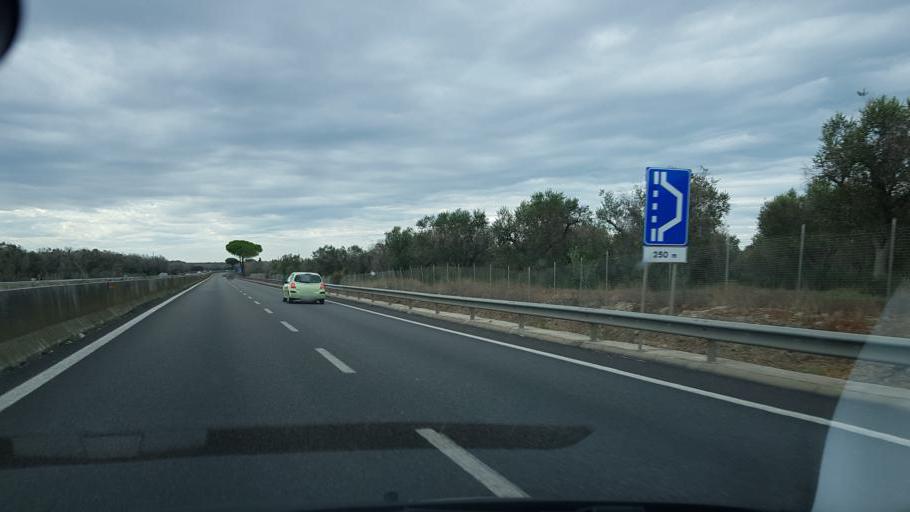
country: IT
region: Apulia
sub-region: Provincia di Lecce
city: Squinzano
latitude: 40.4492
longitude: 18.0696
